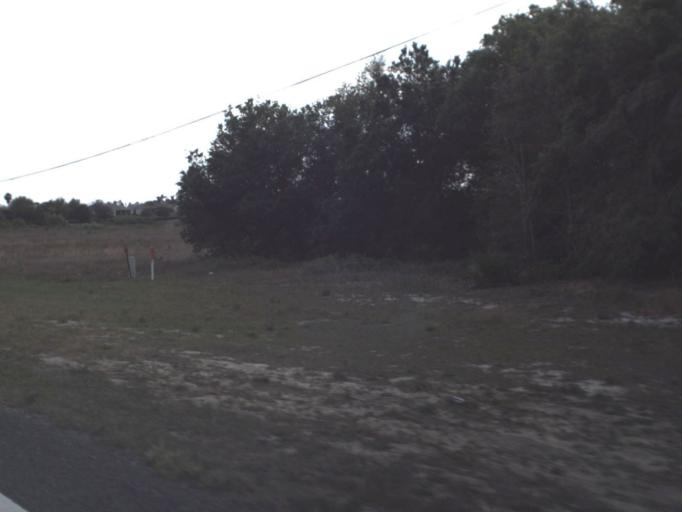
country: US
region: Florida
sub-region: Lake County
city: Hawthorne
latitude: 28.7026
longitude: -81.8584
